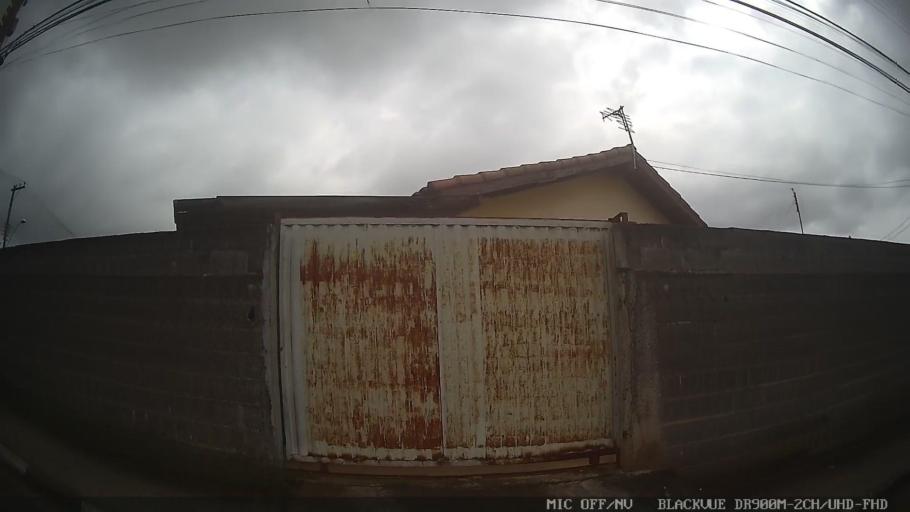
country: BR
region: Sao Paulo
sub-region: Atibaia
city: Atibaia
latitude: -23.1281
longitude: -46.5881
